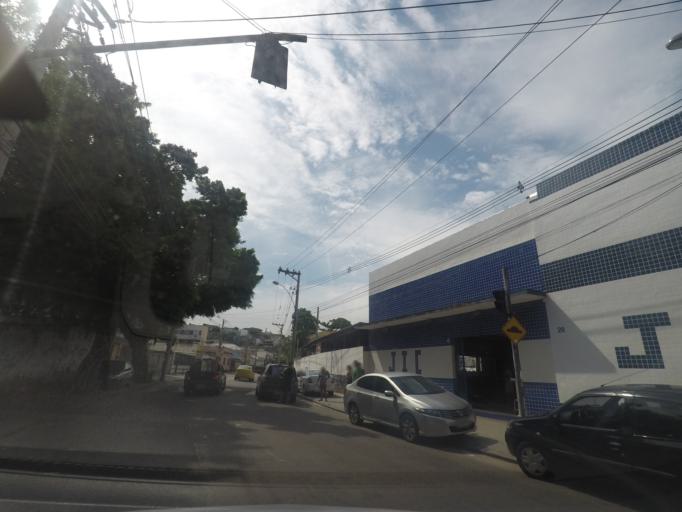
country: BR
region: Rio de Janeiro
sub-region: Rio De Janeiro
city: Rio de Janeiro
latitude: -22.8212
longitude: -43.1743
